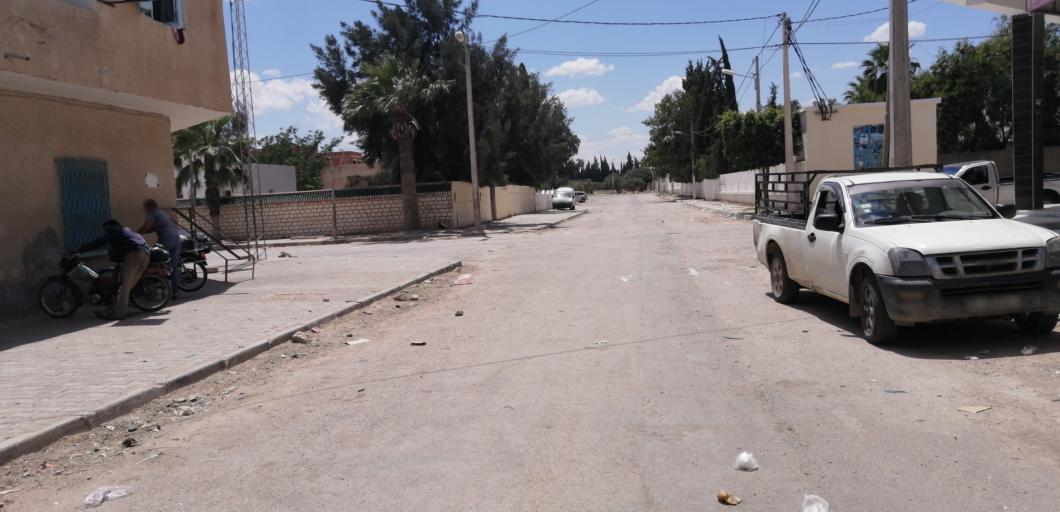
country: TN
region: Al Qayrawan
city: Kairouan
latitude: 35.6170
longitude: 9.9265
